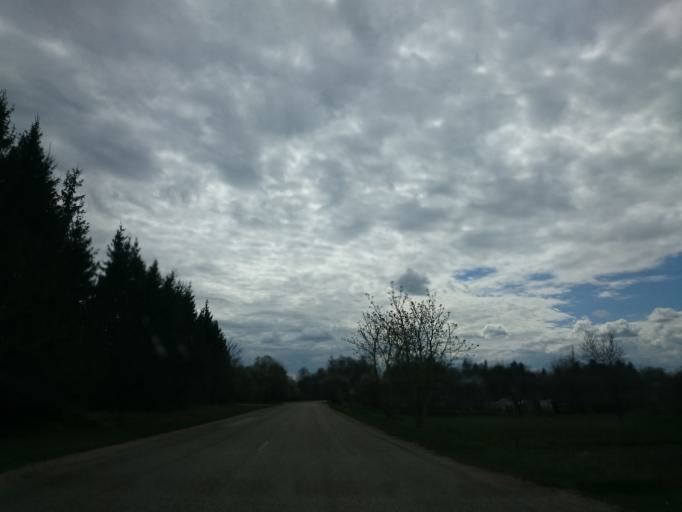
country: LV
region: Aizpute
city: Aizpute
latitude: 56.7392
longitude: 21.6083
